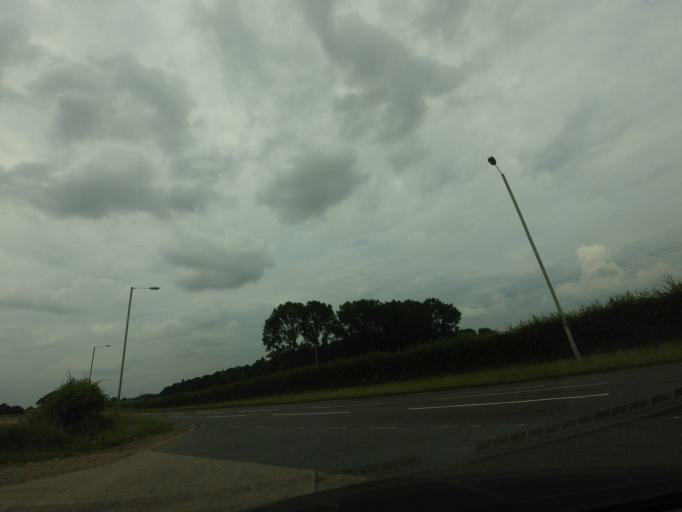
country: GB
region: England
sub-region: Shropshire
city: Tong
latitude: 52.6708
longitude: -2.3094
